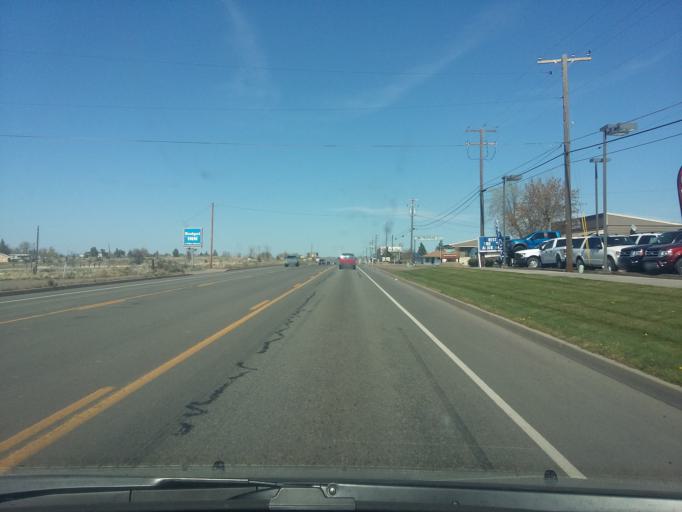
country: US
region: Oregon
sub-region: Jefferson County
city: Madras
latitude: 44.6110
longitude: -121.1371
